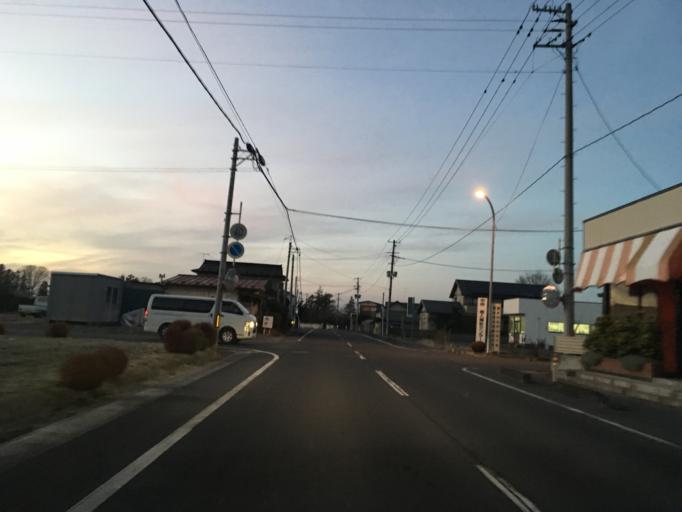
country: JP
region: Miyagi
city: Wakuya
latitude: 38.7114
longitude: 141.2349
